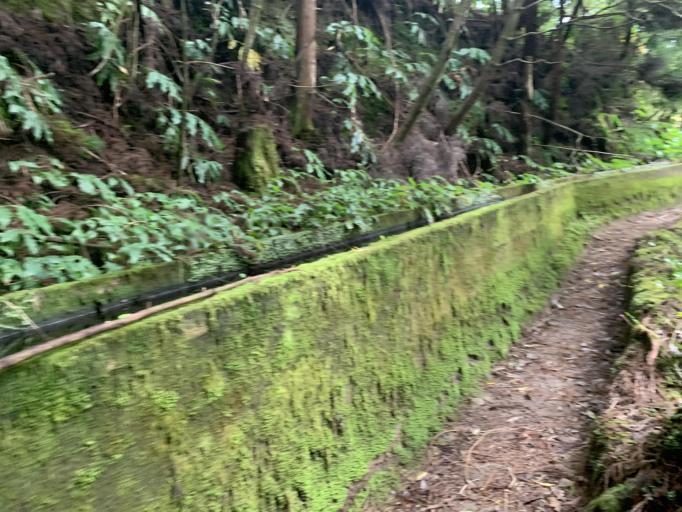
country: PT
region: Azores
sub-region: Vila Franca do Campo
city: Vila Franca do Campo
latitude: 37.7454
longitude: -25.4760
